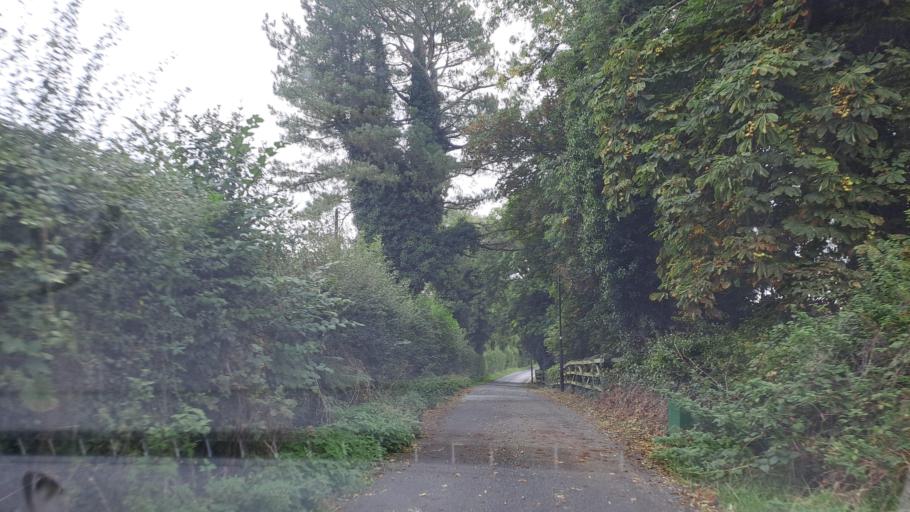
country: IE
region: Ulster
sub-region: An Cabhan
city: Kingscourt
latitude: 53.9538
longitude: -6.7767
